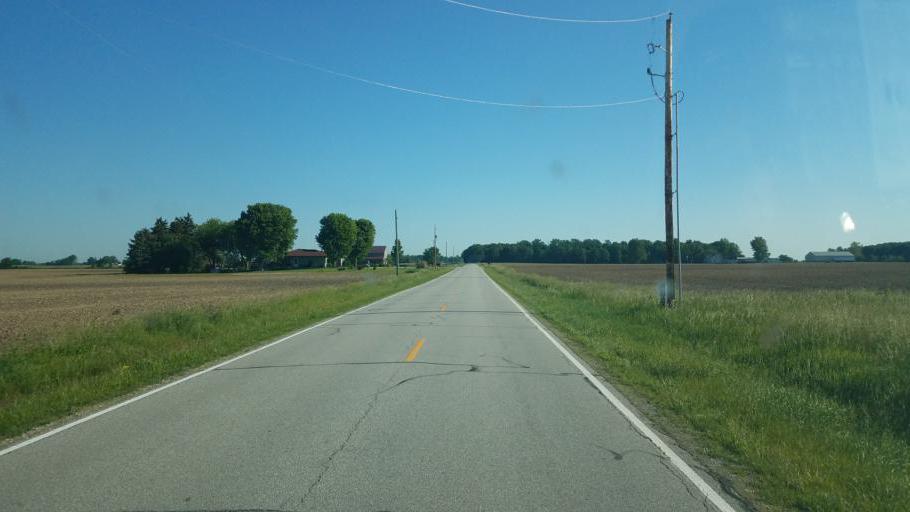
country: US
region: Ohio
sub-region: Crawford County
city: Bucyrus
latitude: 40.7251
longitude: -82.9531
